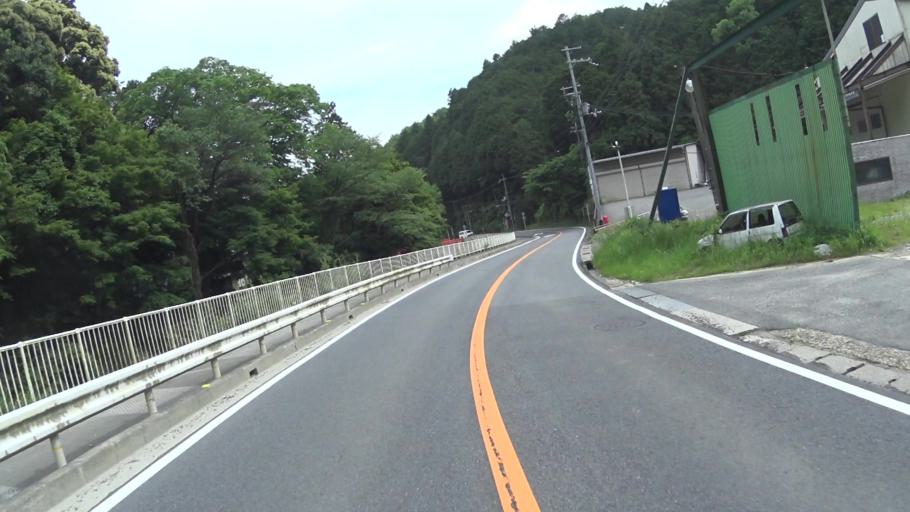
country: JP
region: Shiga Prefecture
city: Kitahama
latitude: 35.1608
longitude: 135.8652
